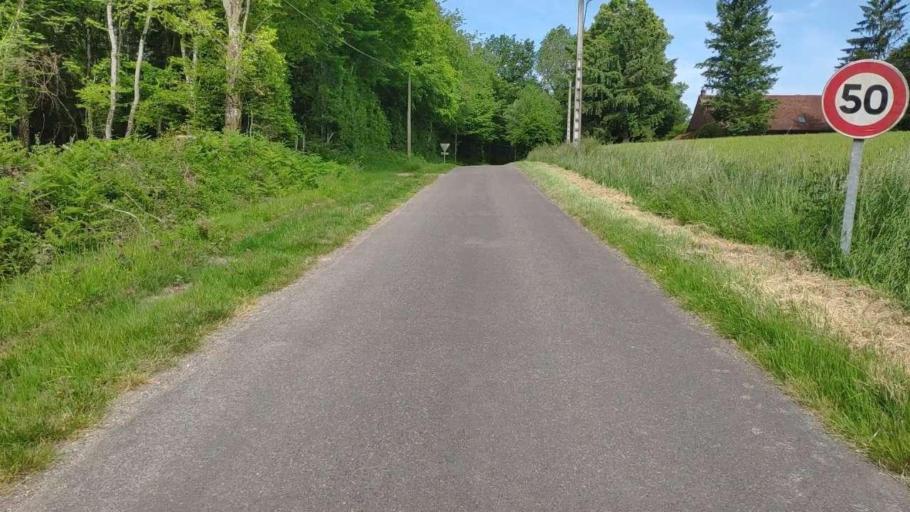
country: FR
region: Franche-Comte
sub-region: Departement du Jura
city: Bletterans
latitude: 46.6754
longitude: 5.4162
